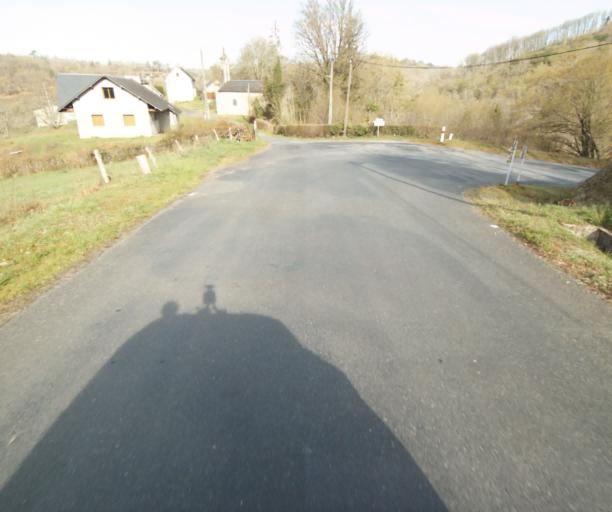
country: FR
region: Limousin
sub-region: Departement de la Correze
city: Correze
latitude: 45.3413
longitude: 1.8223
